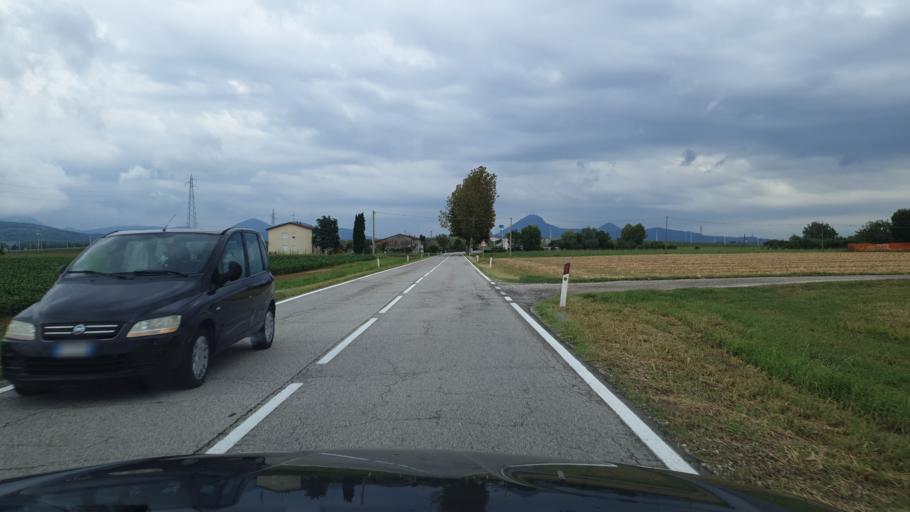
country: IT
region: Veneto
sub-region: Provincia di Vicenza
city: Noventa Vicentina
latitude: 45.2748
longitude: 11.5642
